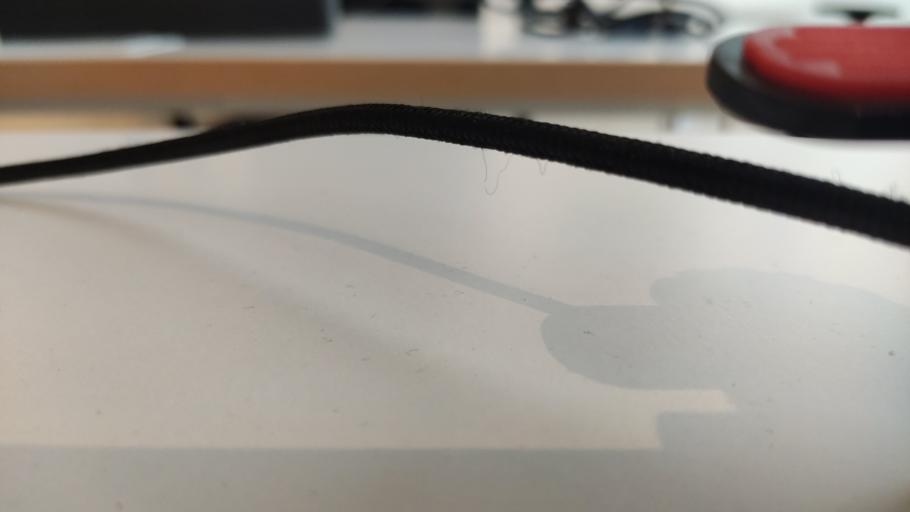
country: RU
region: Moskovskaya
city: Shevlyakovo
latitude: 56.3994
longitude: 36.8644
